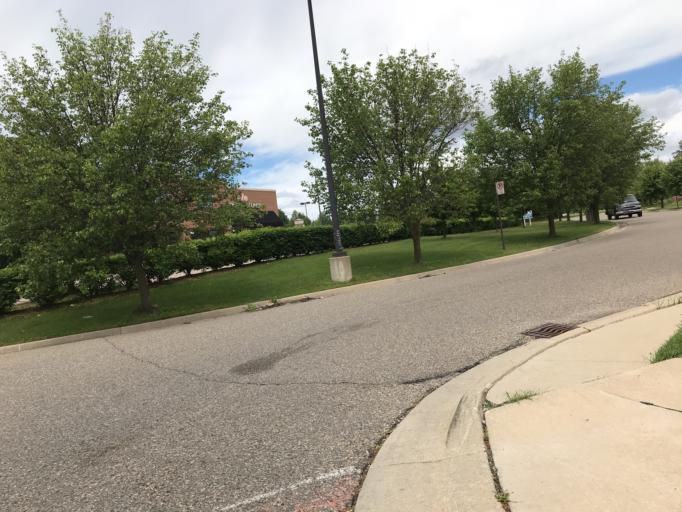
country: US
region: Michigan
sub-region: Oakland County
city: Farmington Hills
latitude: 42.5245
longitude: -83.3529
